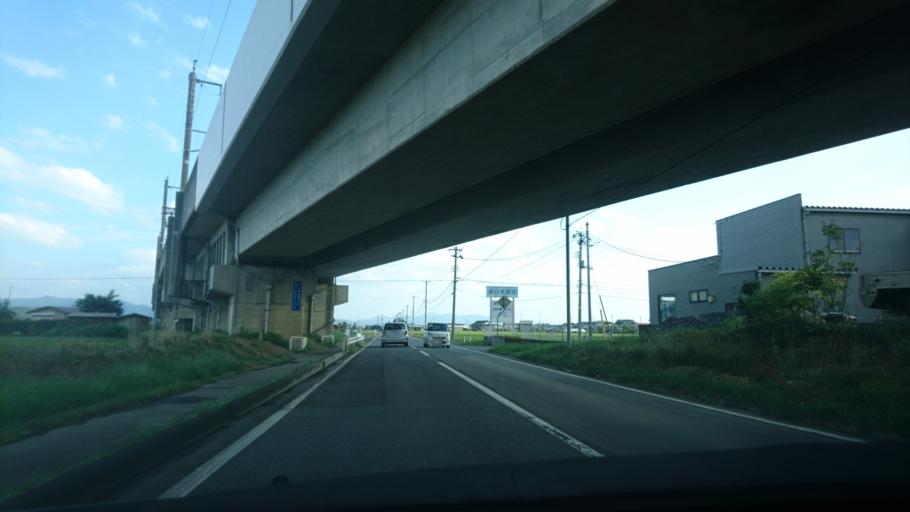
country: JP
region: Iwate
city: Mizusawa
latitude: 39.1730
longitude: 141.1777
